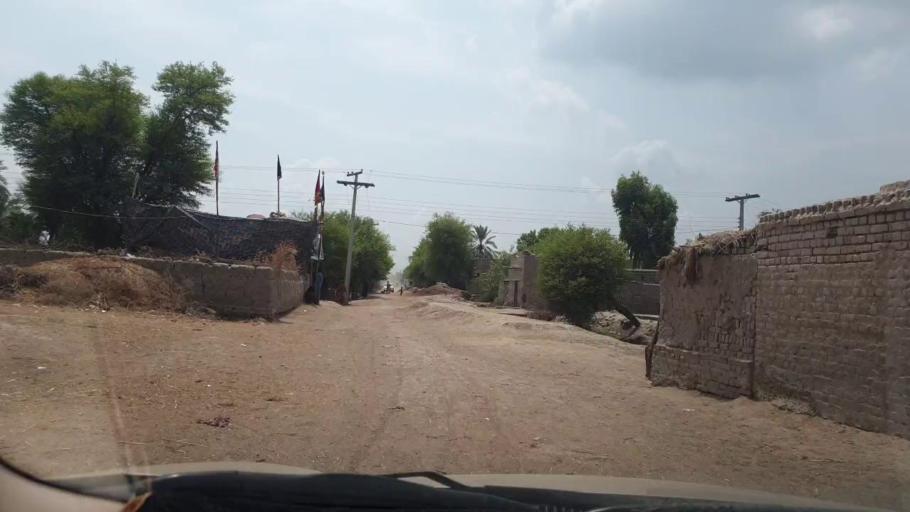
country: PK
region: Sindh
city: Larkana
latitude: 27.6090
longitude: 68.1303
